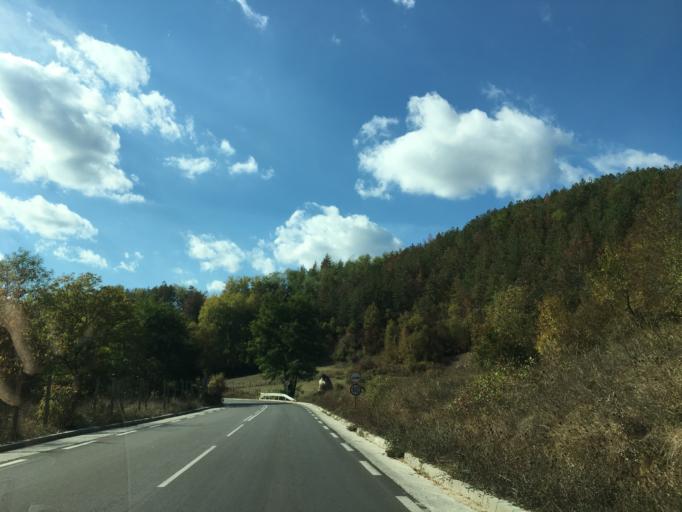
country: BG
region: Smolyan
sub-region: Obshtina Zlatograd
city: Zlatograd
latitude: 41.3952
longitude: 25.0793
